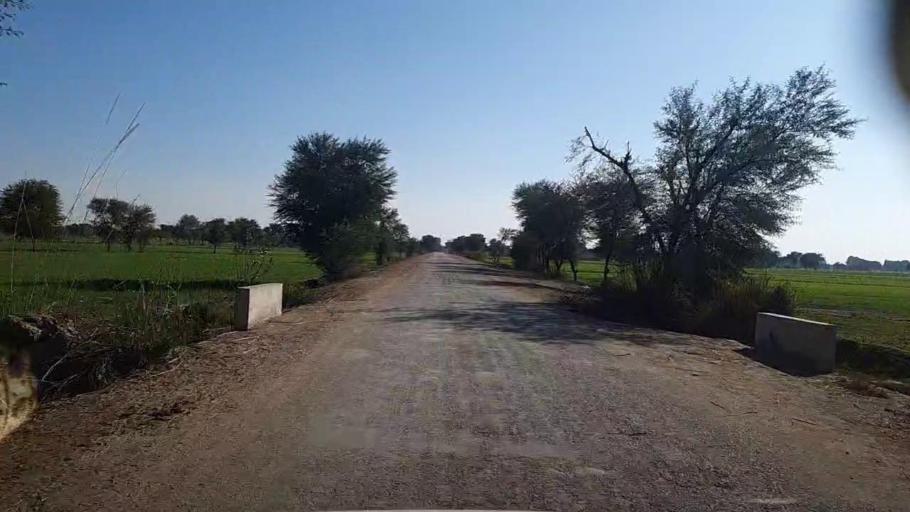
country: PK
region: Sindh
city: Khairpur
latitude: 27.9172
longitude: 69.7515
